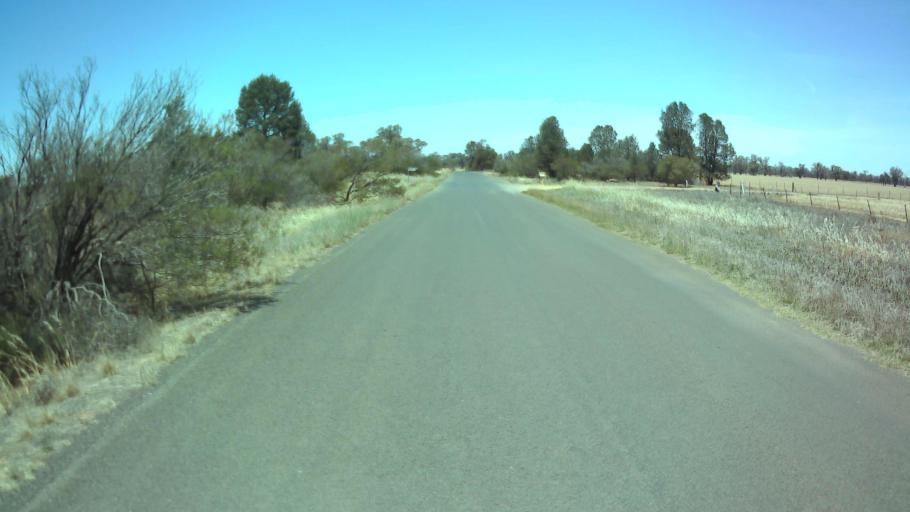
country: AU
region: New South Wales
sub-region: Weddin
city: Grenfell
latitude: -34.0569
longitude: 147.7804
